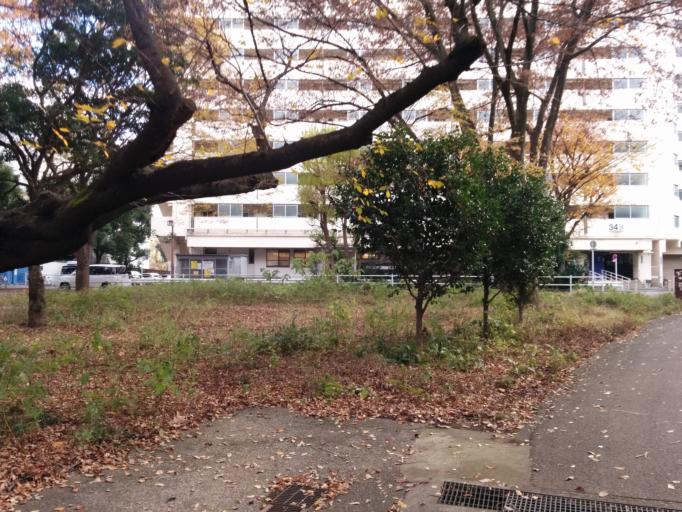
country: JP
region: Tokyo
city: Tokyo
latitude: 35.7029
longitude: 139.7105
